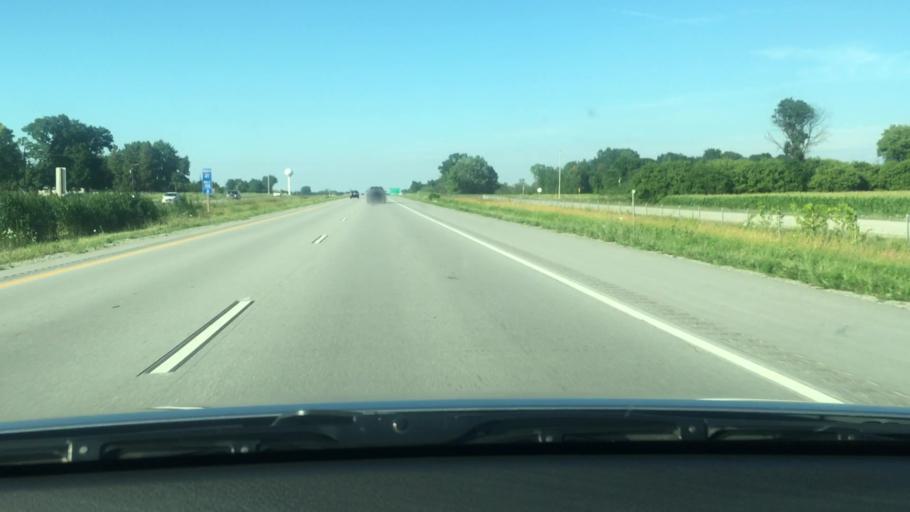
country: US
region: Wisconsin
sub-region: Brown County
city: Wrightstown
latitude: 44.4052
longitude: -88.1440
